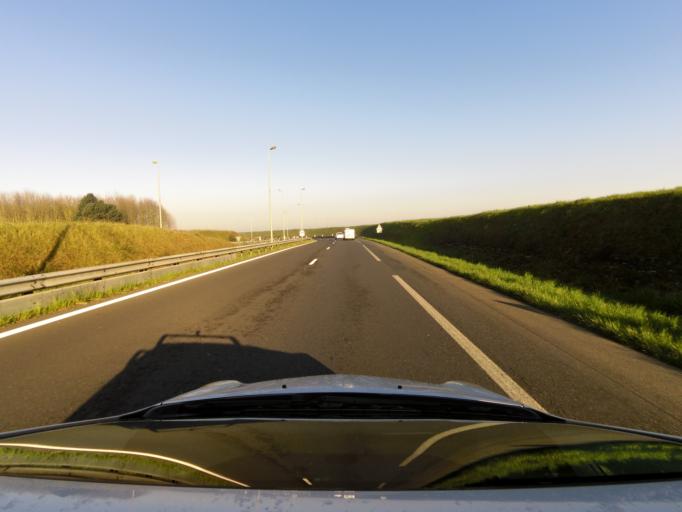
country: FR
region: Lower Normandy
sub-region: Departement du Calvados
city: Saint-Germain-la-Blanche-Herbe
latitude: 49.1914
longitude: -0.4205
